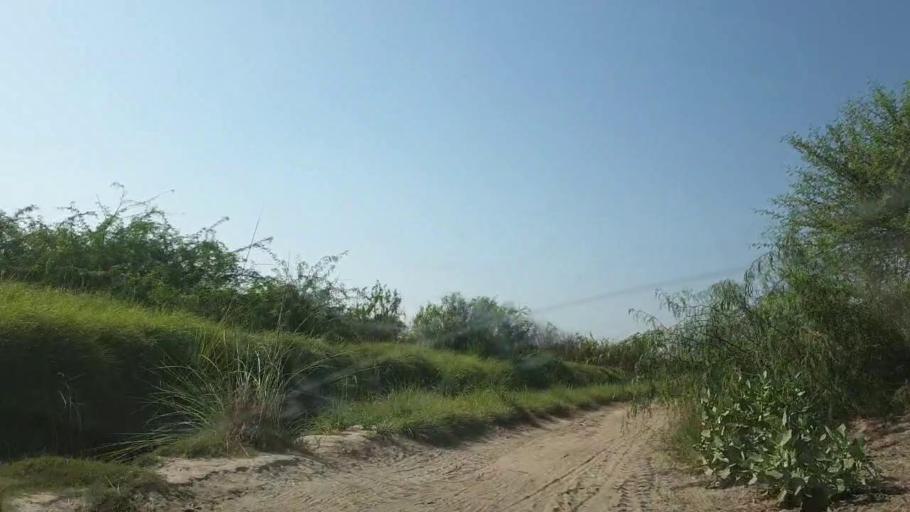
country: PK
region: Sindh
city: Tando Jam
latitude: 25.3213
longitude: 68.5992
